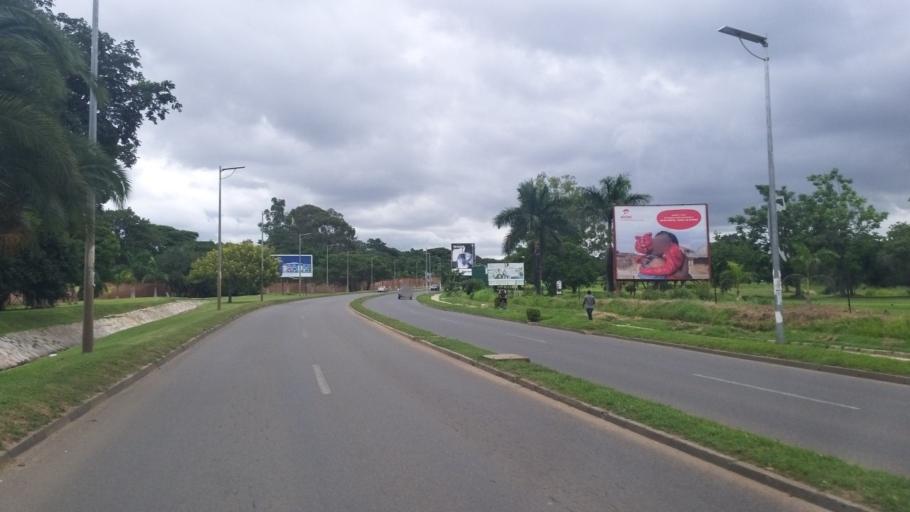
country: ZM
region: Lusaka
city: Lusaka
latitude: -15.4241
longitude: 28.3292
